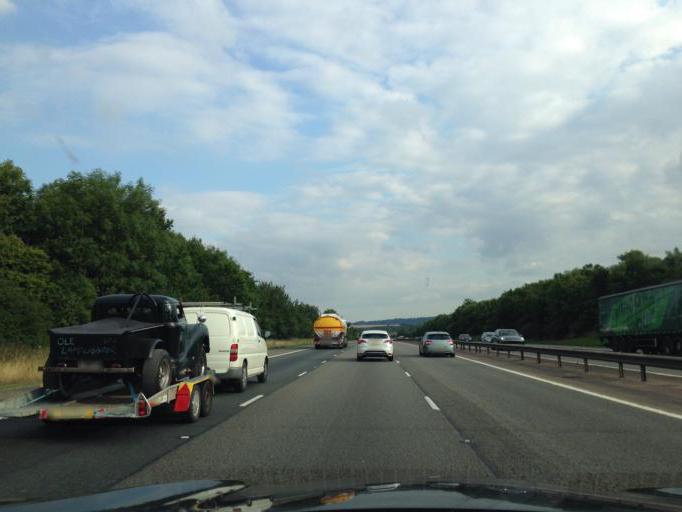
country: GB
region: England
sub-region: Warwickshire
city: Harbury
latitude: 52.1813
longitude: -1.4472
